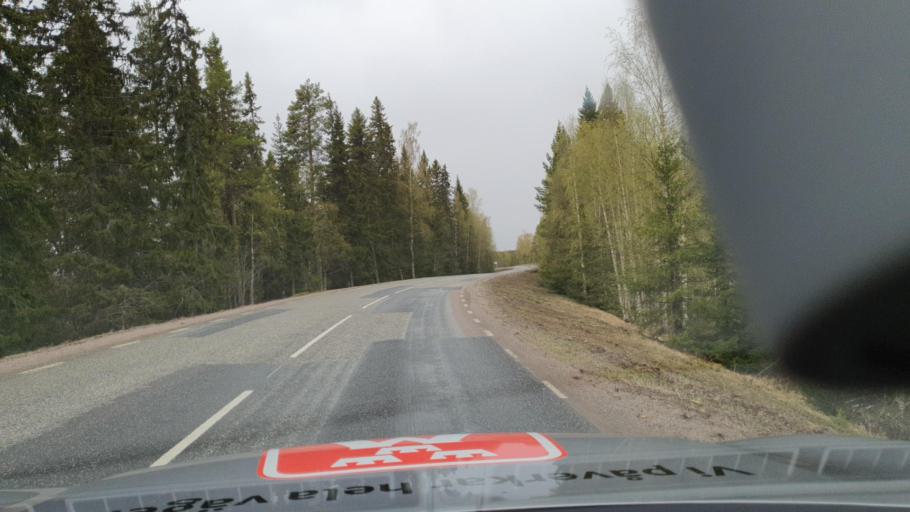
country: SE
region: Vaesternorrland
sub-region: Solleftea Kommun
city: Solleftea
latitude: 63.6531
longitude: 17.2890
